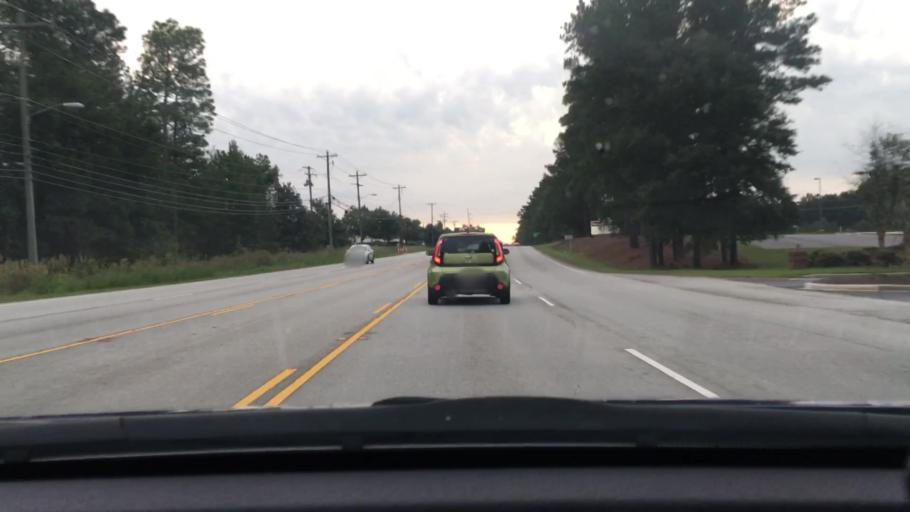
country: US
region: South Carolina
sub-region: Lexington County
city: Saint Andrews
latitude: 34.0782
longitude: -81.1285
